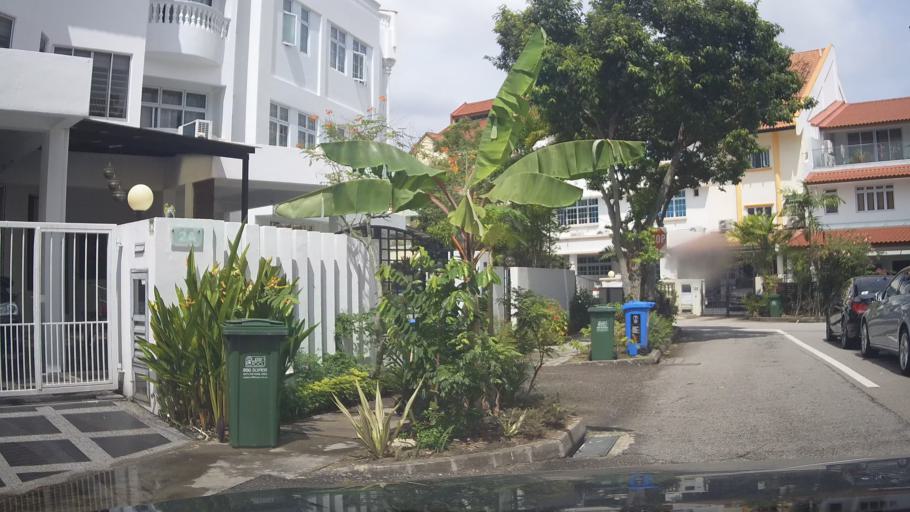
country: SG
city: Singapore
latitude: 1.3145
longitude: 103.9030
